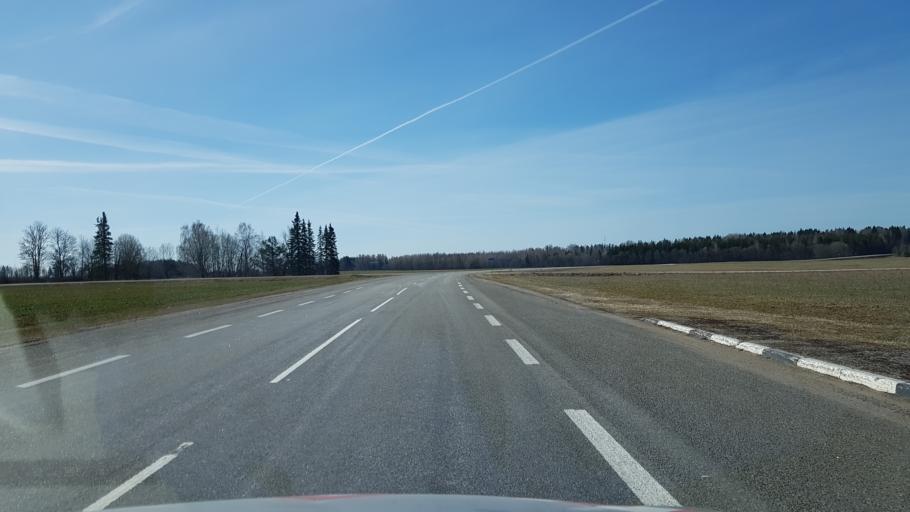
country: EE
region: Laeaene-Virumaa
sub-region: Tamsalu vald
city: Tamsalu
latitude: 59.1860
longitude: 26.1848
